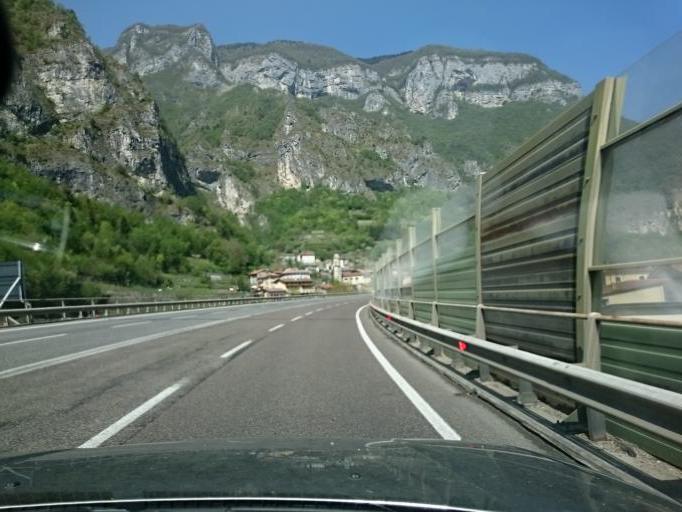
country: IT
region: Veneto
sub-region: Provincia di Vicenza
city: Cismon del Grappa
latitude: 45.8970
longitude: 11.6910
